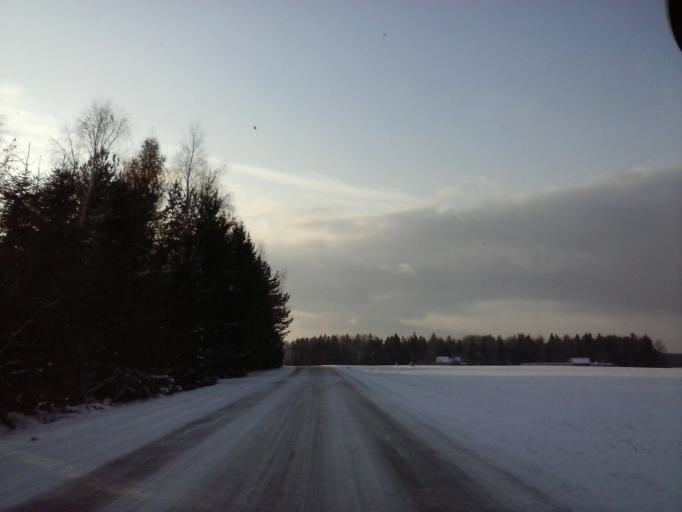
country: EE
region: Tartu
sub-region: UElenurme vald
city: Ulenurme
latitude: 58.3213
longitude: 26.8766
